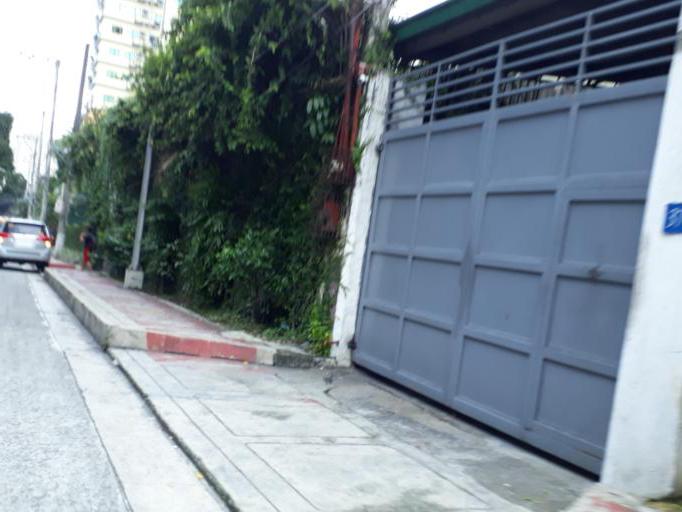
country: PH
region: Metro Manila
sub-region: San Juan
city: San Juan
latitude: 14.6140
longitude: 121.0365
